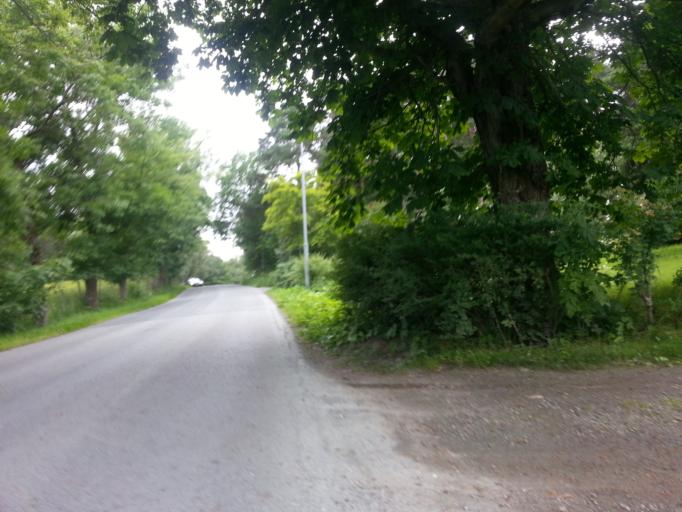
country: NO
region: Sor-Trondelag
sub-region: Trondheim
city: Trondheim
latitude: 63.4345
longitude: 10.4789
